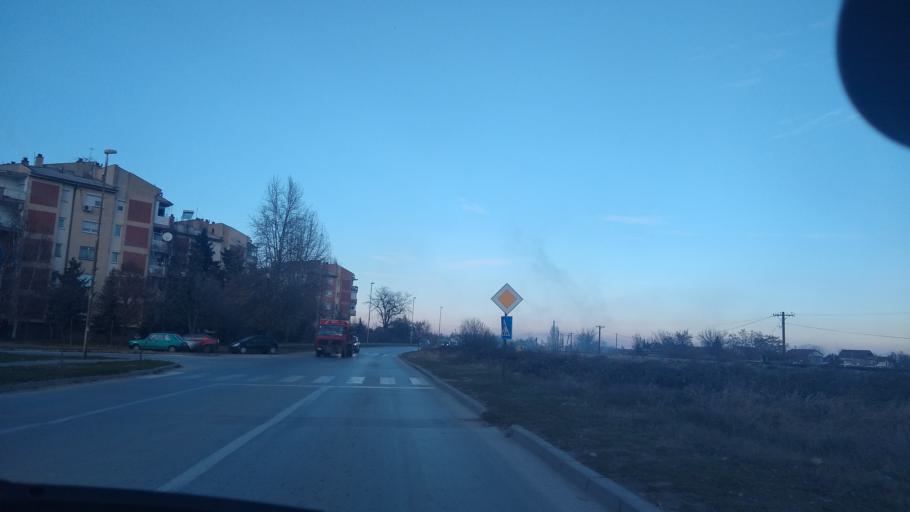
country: MK
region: Bitola
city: Bitola
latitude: 41.0277
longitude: 21.3461
